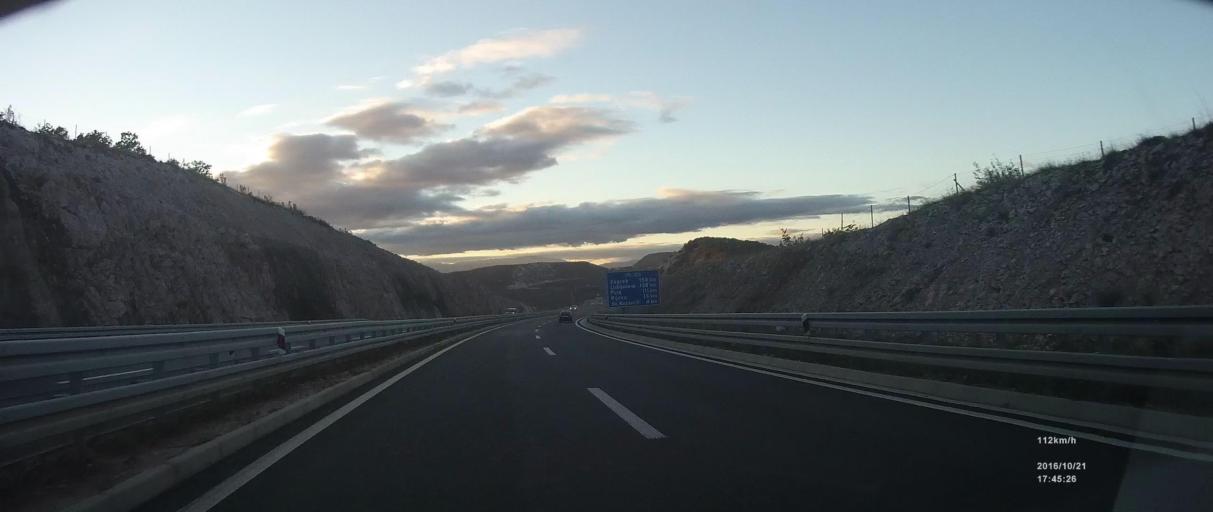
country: HR
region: Primorsko-Goranska
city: Kraljevica
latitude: 45.2906
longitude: 14.5778
